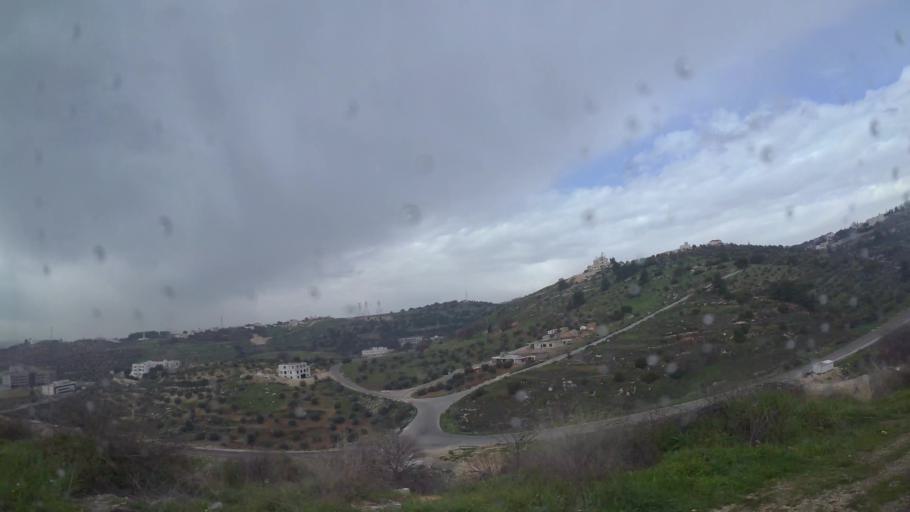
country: JO
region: Amman
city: Wadi as Sir
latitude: 31.9870
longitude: 35.8164
